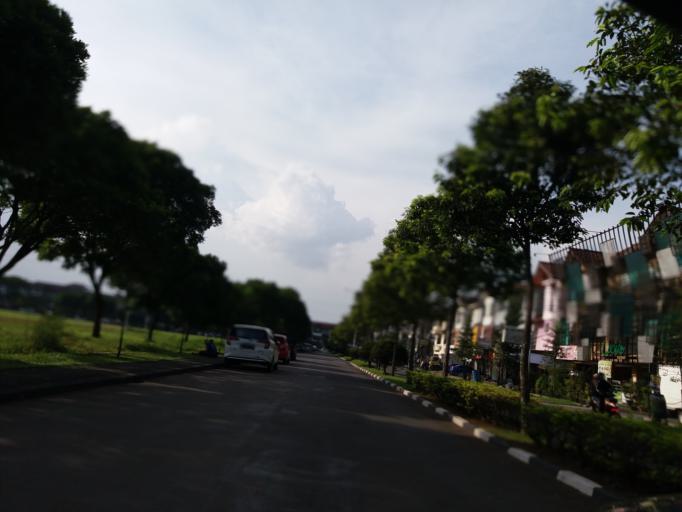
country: ID
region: West Java
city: Bandung
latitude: -6.9560
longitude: 107.6284
